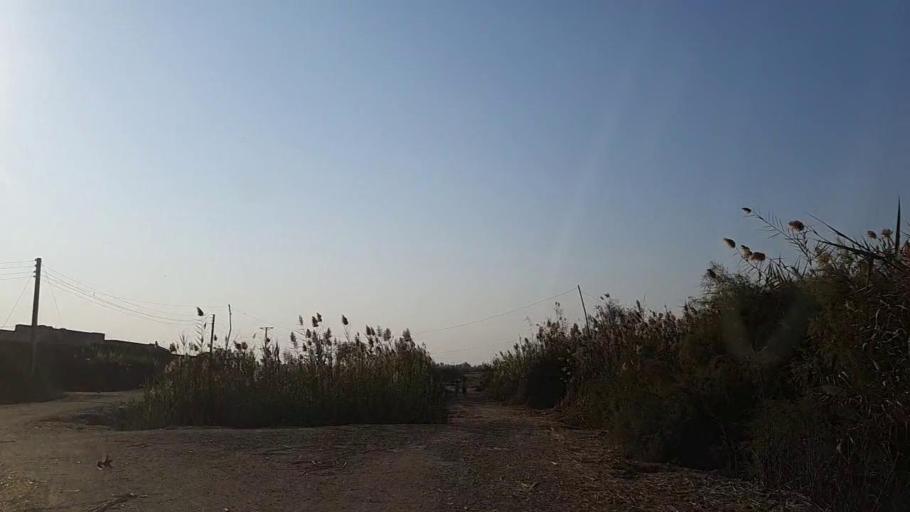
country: PK
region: Sindh
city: Daur
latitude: 26.4172
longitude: 68.3548
